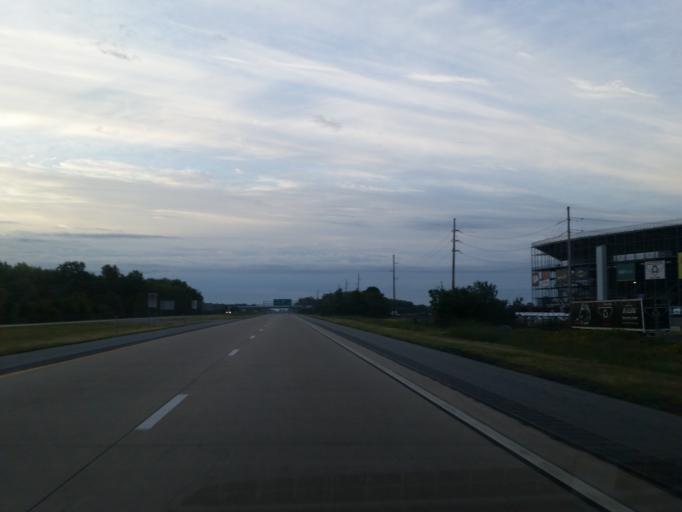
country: US
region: Delaware
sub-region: Kent County
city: Dover
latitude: 39.1961
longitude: -75.5316
